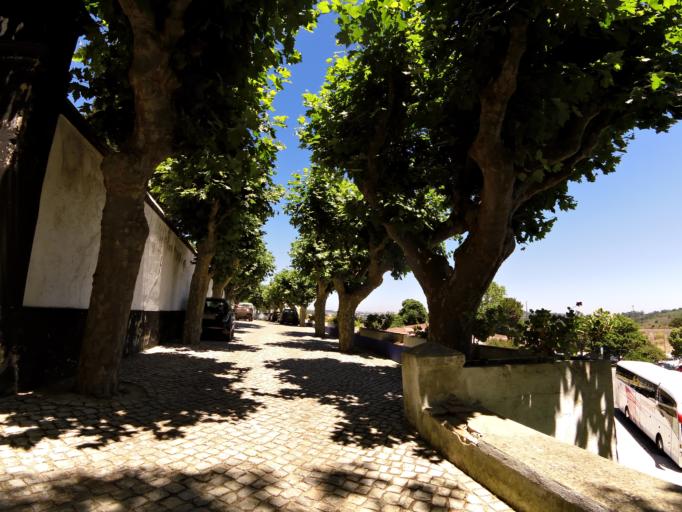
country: PT
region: Leiria
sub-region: Obidos
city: Obidos
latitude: 39.3579
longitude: -9.1586
